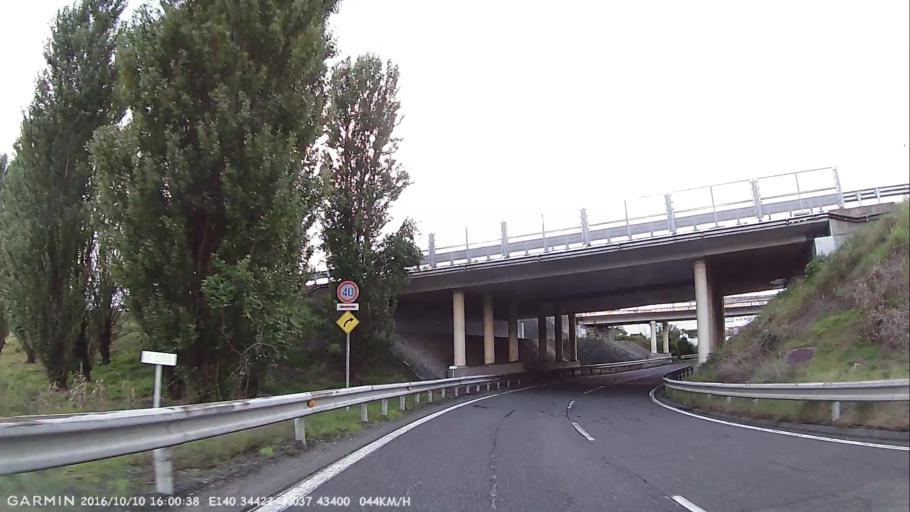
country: JP
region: Fukushima
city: Koriyama
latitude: 37.4340
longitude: 140.3448
